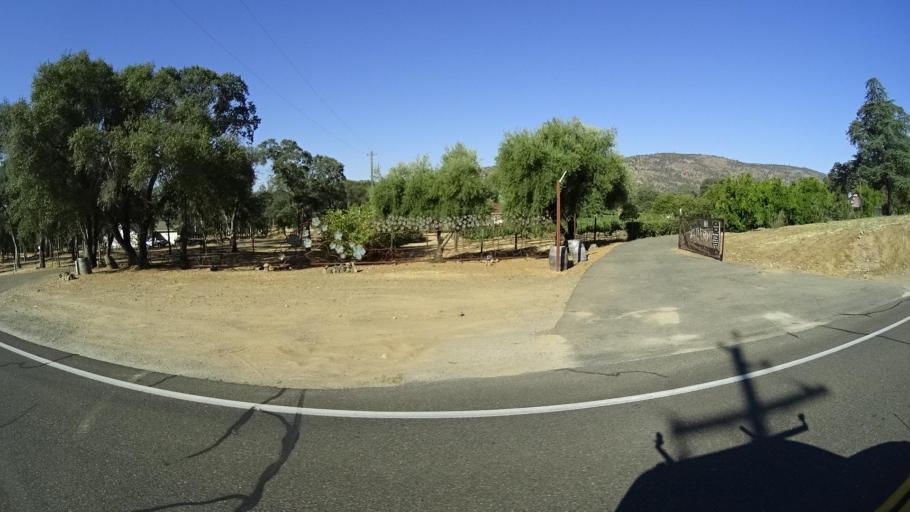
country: US
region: California
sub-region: Mariposa County
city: Mariposa
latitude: 37.5480
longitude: -120.0979
